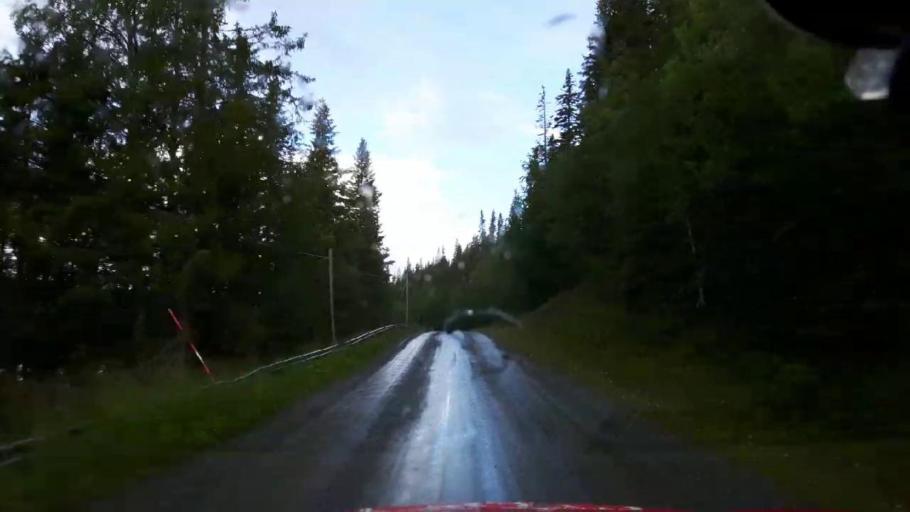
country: NO
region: Nordland
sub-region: Hattfjelldal
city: Hattfjelldal
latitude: 64.8645
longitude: 14.9030
